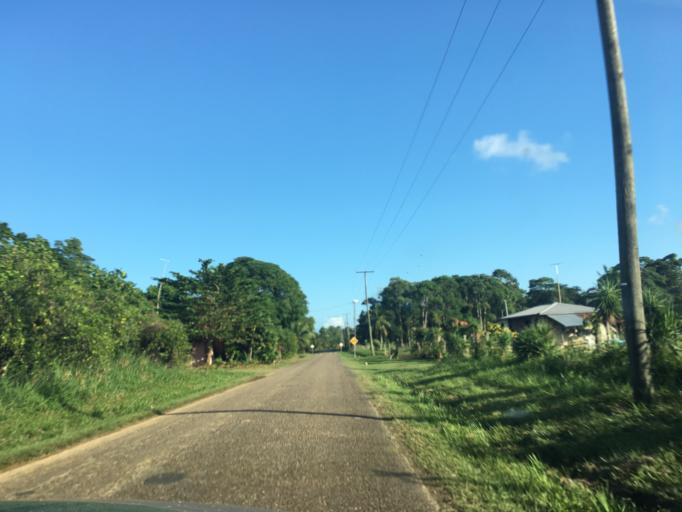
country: BZ
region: Stann Creek
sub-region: Dangriga
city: Dangriga
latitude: 16.8198
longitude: -88.3340
